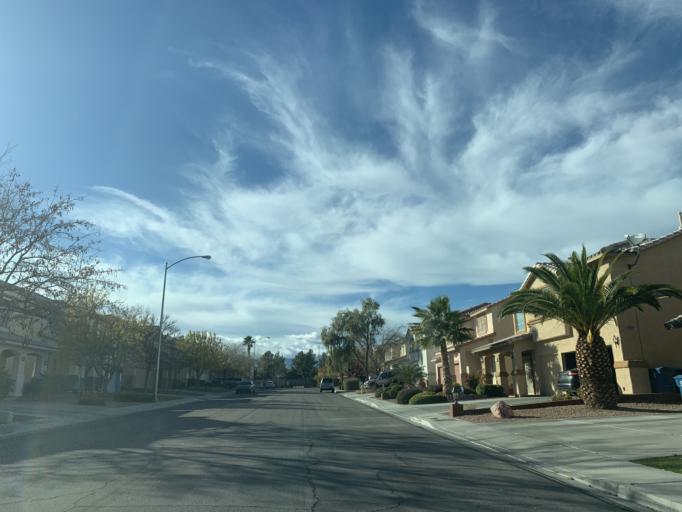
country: US
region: Nevada
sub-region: Clark County
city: Summerlin South
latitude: 36.1266
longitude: -115.3036
